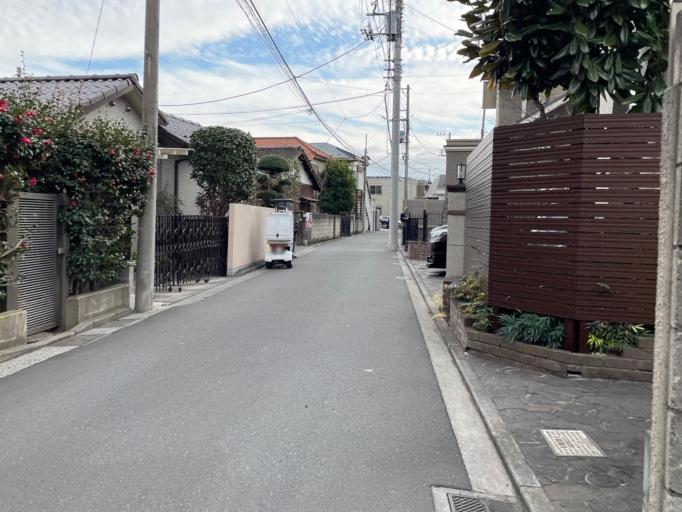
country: JP
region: Tokyo
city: Kamirenjaku
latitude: 35.7041
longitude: 139.5401
